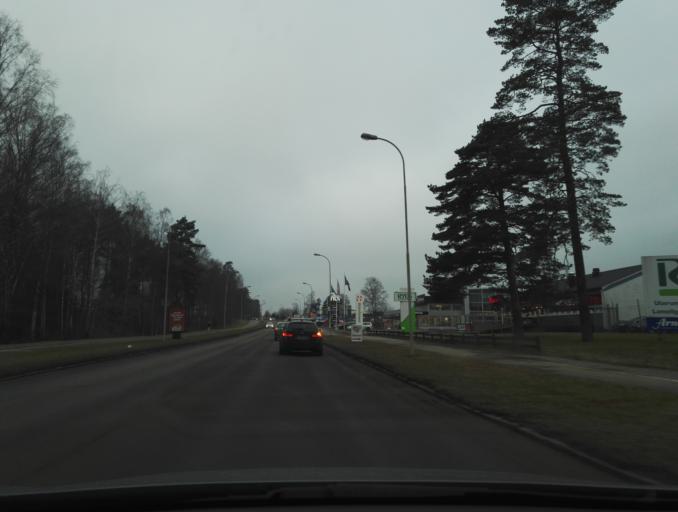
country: SE
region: Kronoberg
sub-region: Vaxjo Kommun
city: Vaexjoe
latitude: 56.8877
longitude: 14.7773
